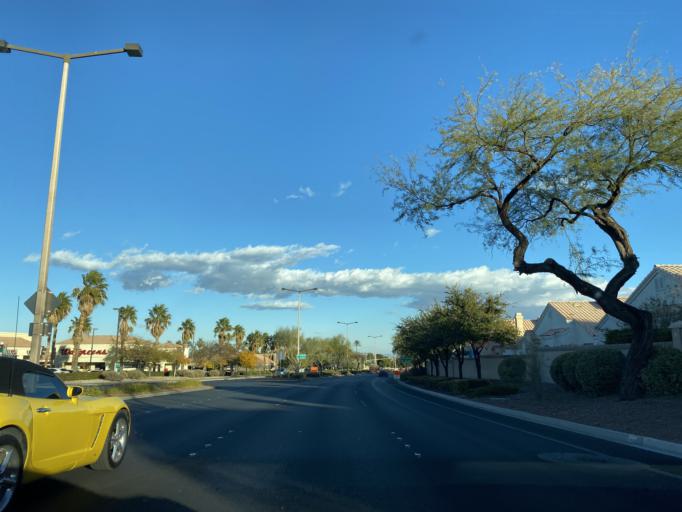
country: US
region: Nevada
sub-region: Clark County
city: Summerlin South
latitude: 36.2061
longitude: -115.3033
